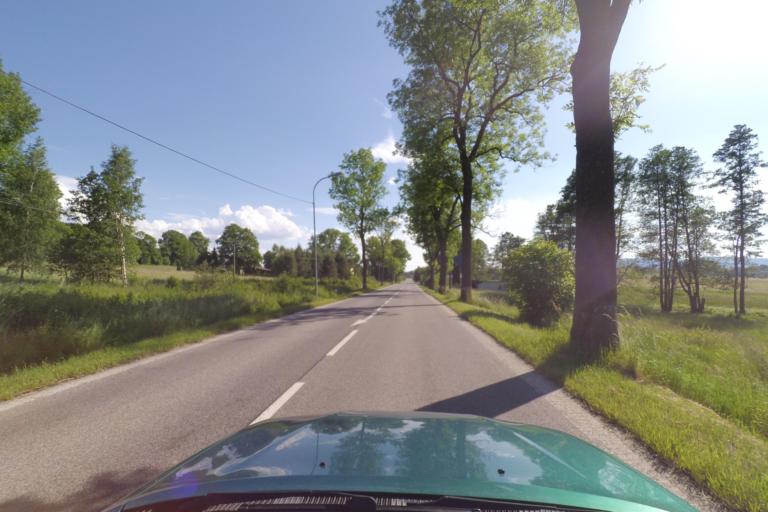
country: PL
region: Lower Silesian Voivodeship
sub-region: Powiat kamiennogorski
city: Lubawka
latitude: 50.6845
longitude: 15.9812
